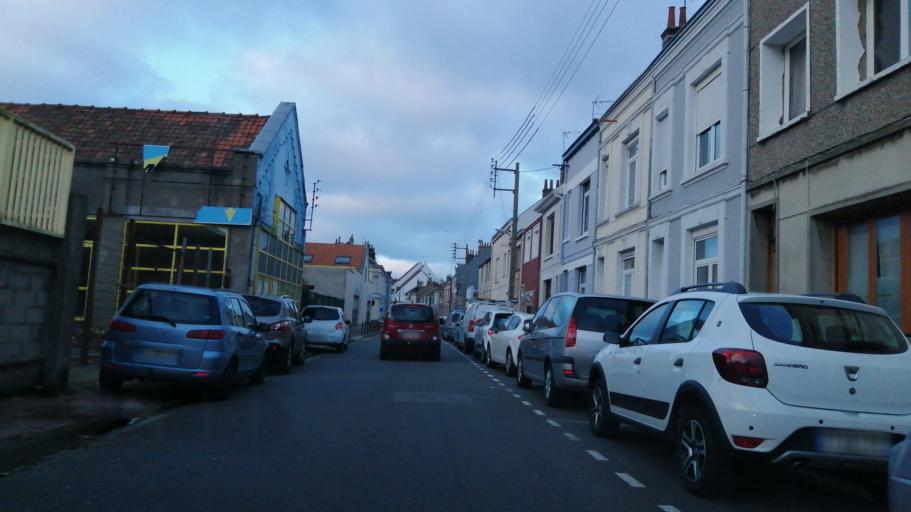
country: FR
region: Nord-Pas-de-Calais
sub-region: Departement du Pas-de-Calais
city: Calais
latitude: 50.9401
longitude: 1.8611
